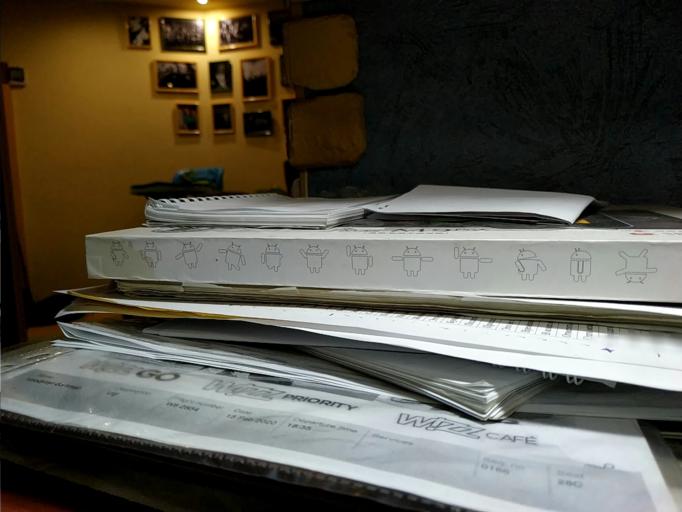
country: RU
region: Arkhangelskaya
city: Kargopol'
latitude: 61.6079
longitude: 39.2597
